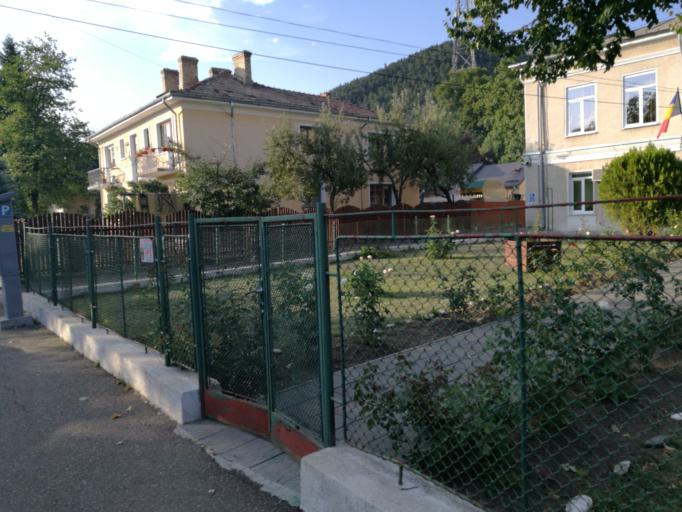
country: RO
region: Neamt
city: Piatra Neamt
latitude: 46.9341
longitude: 26.3638
